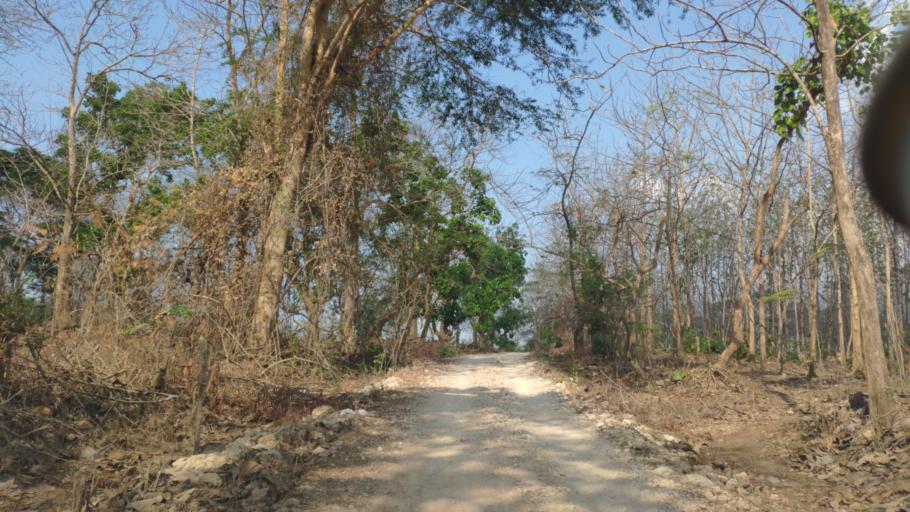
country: ID
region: East Java
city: Ngrowo
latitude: -7.0782
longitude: 111.5913
